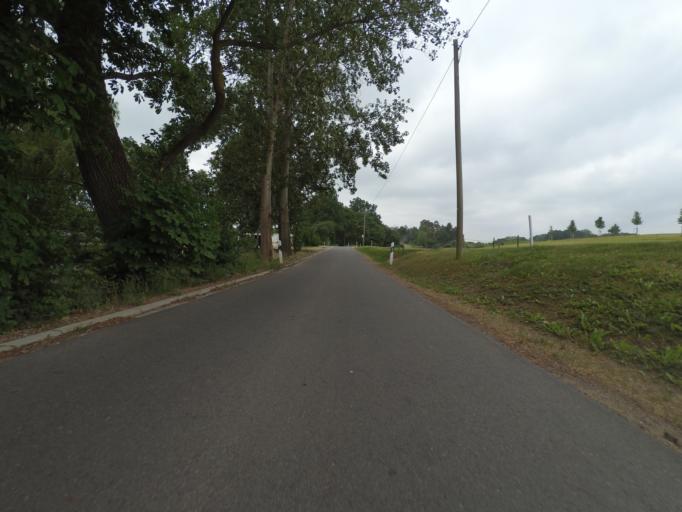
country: DE
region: Mecklenburg-Vorpommern
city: Krakow am See
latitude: 53.6543
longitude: 12.3439
